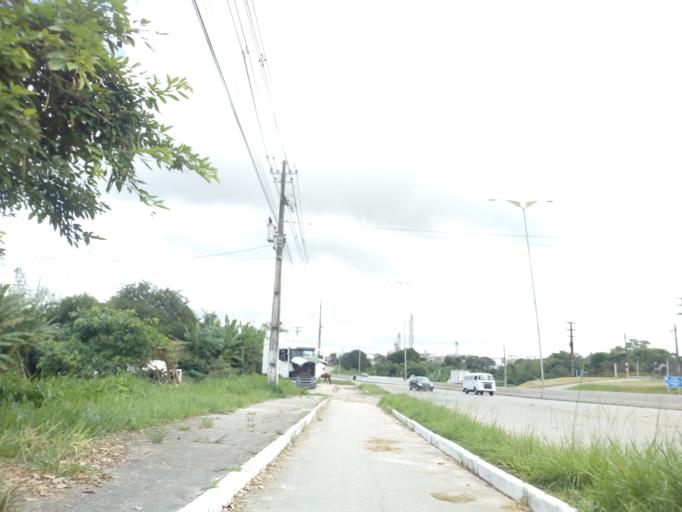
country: BR
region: Pernambuco
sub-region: Cabo De Santo Agostinho
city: Cabo
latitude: -8.2745
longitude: -35.0264
